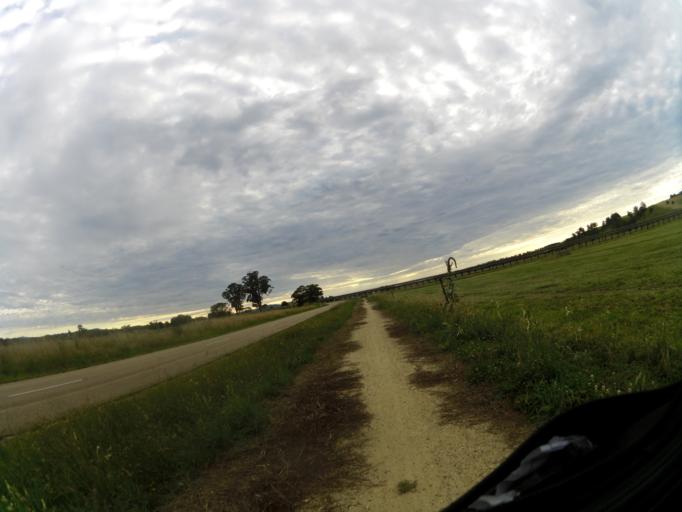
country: AU
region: Victoria
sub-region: East Gippsland
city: Lakes Entrance
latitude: -37.7246
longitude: 148.4441
